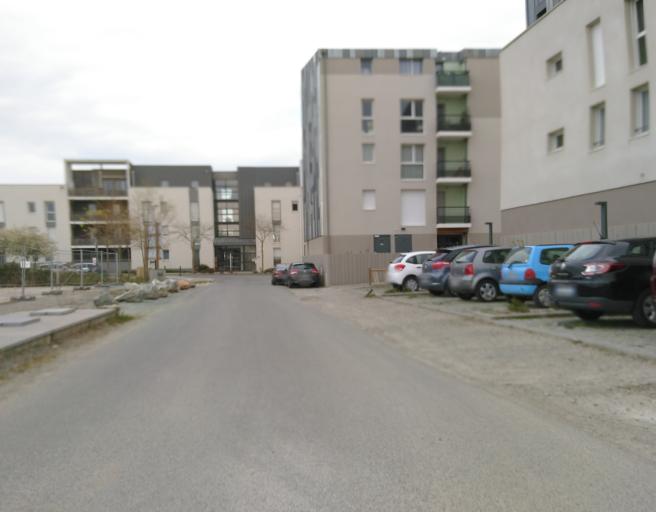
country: FR
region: Pays de la Loire
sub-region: Departement de Maine-et-Loire
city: Les Ponts-de-Ce
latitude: 47.4462
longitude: -0.5127
